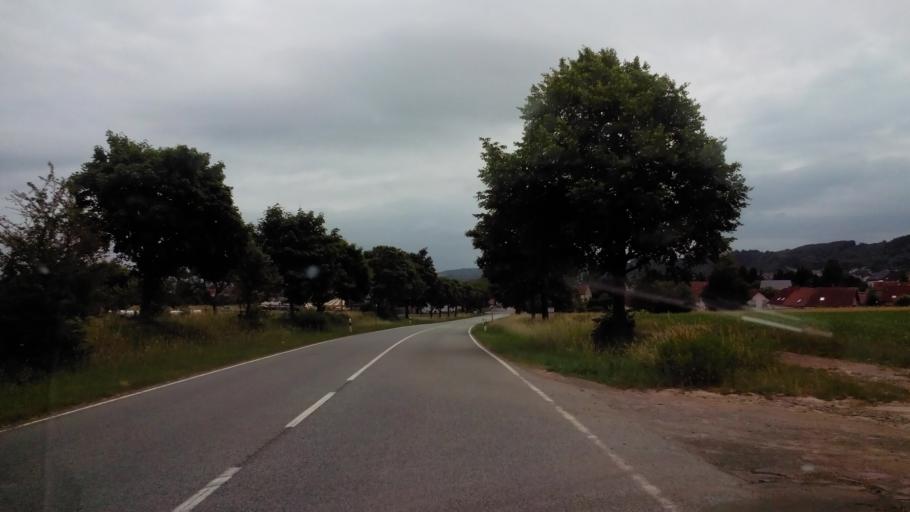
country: DE
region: Saarland
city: Losheim
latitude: 49.5151
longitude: 6.7324
